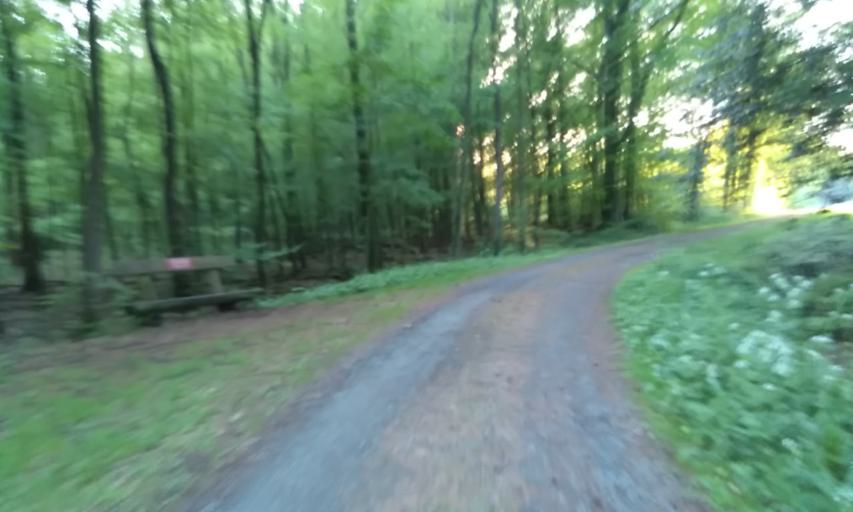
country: DE
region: Lower Saxony
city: Ahlerstedt
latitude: 53.4204
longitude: 9.4831
